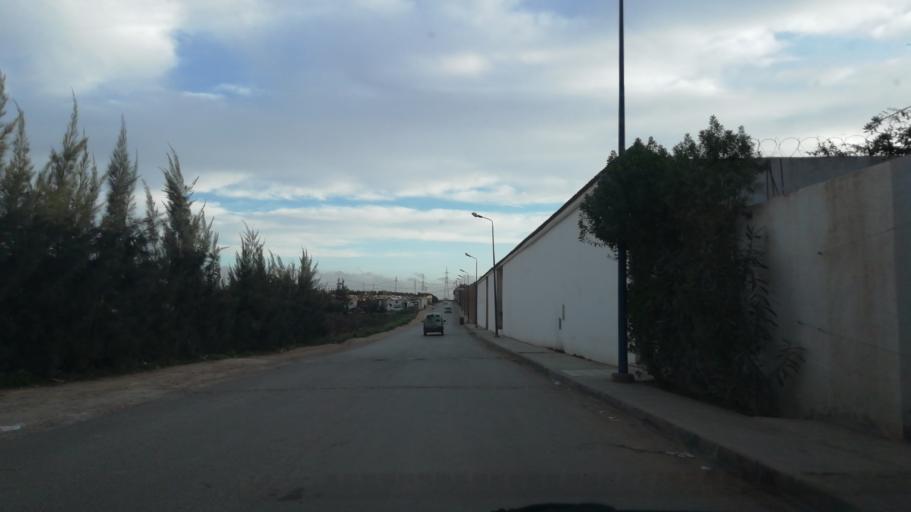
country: DZ
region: Oran
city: Es Senia
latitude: 35.6844
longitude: -0.5870
